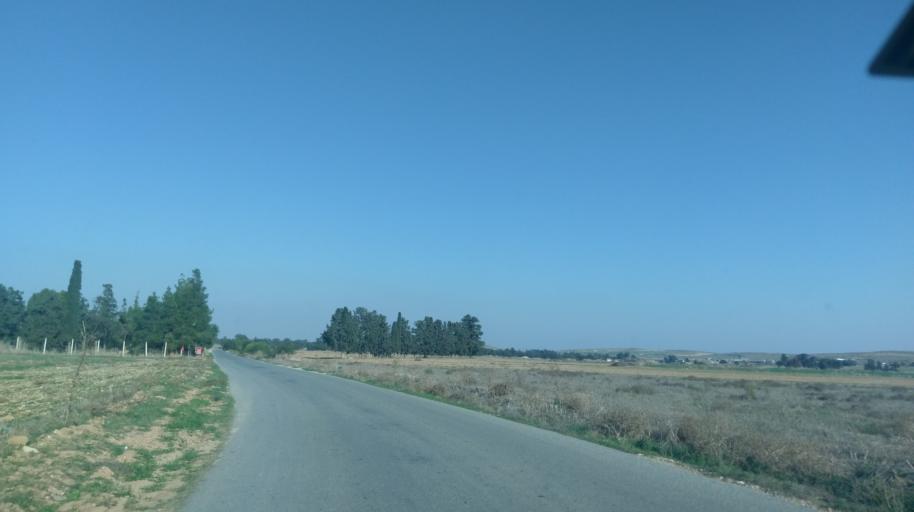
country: CY
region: Larnaka
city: Troulloi
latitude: 35.0833
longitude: 33.6127
